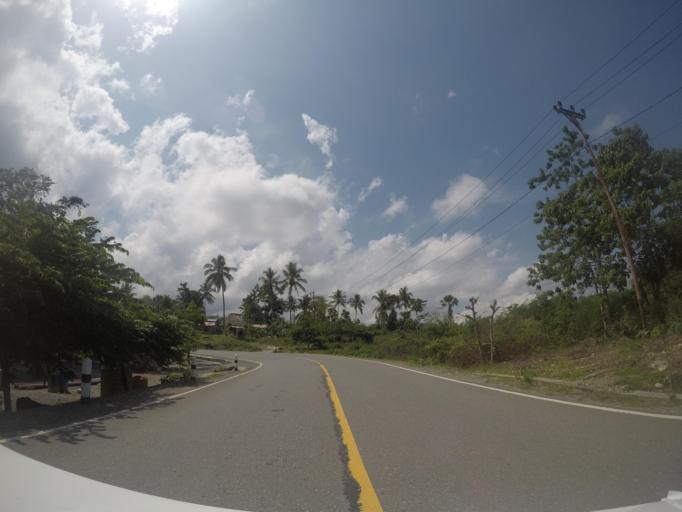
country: TL
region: Baucau
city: Baucau
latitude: -8.4877
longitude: 126.3461
